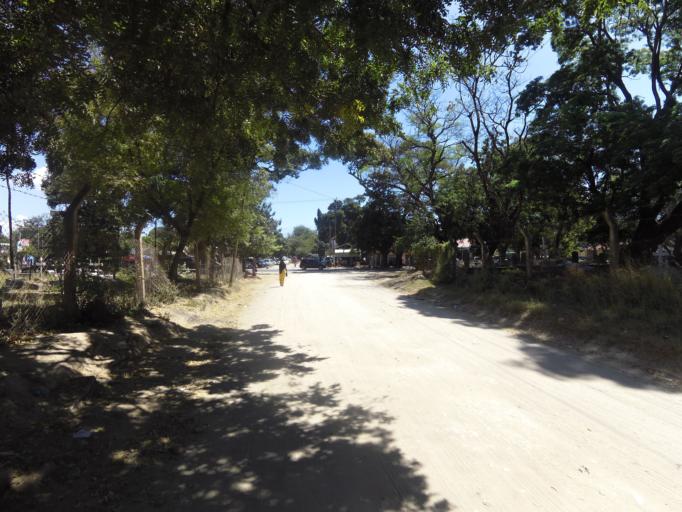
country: TZ
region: Dar es Salaam
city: Magomeni
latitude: -6.7909
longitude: 39.2720
